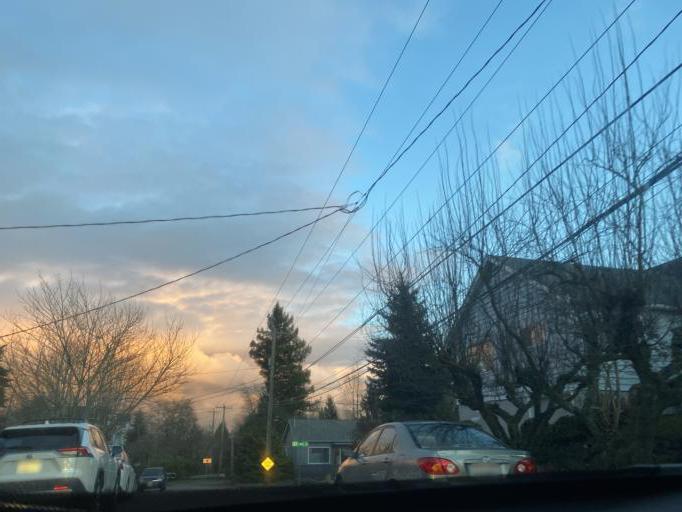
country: US
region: Washington
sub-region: King County
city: Seattle
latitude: 47.6577
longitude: -122.3975
